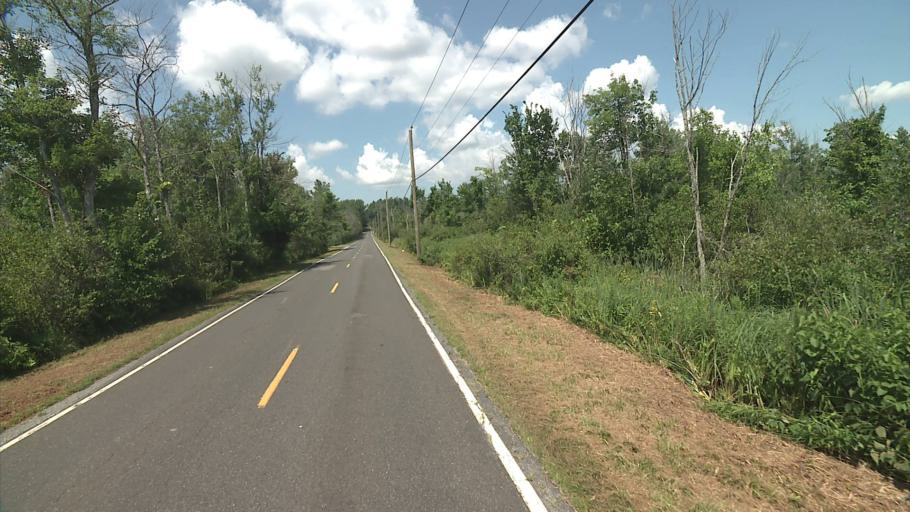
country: US
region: Connecticut
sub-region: Litchfield County
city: Canaan
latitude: 41.9508
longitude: -73.3397
